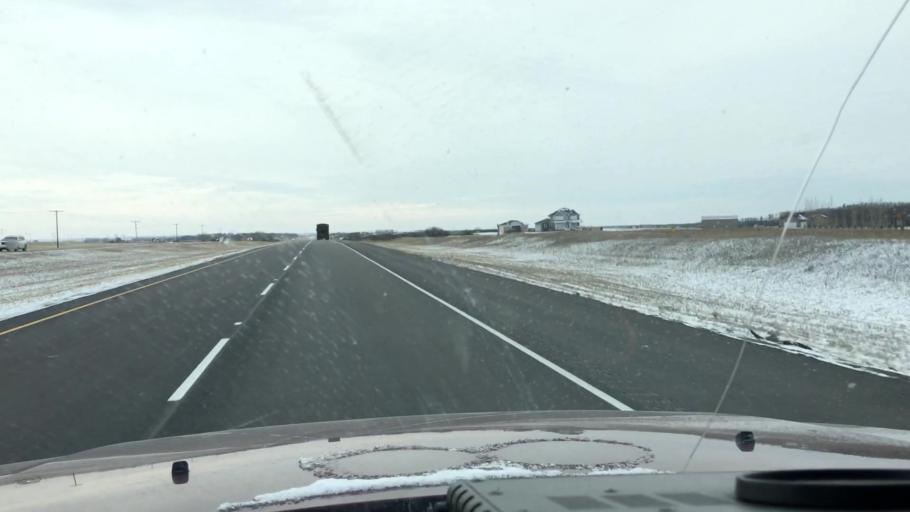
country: CA
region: Saskatchewan
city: Saskatoon
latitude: 51.9304
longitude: -106.5355
